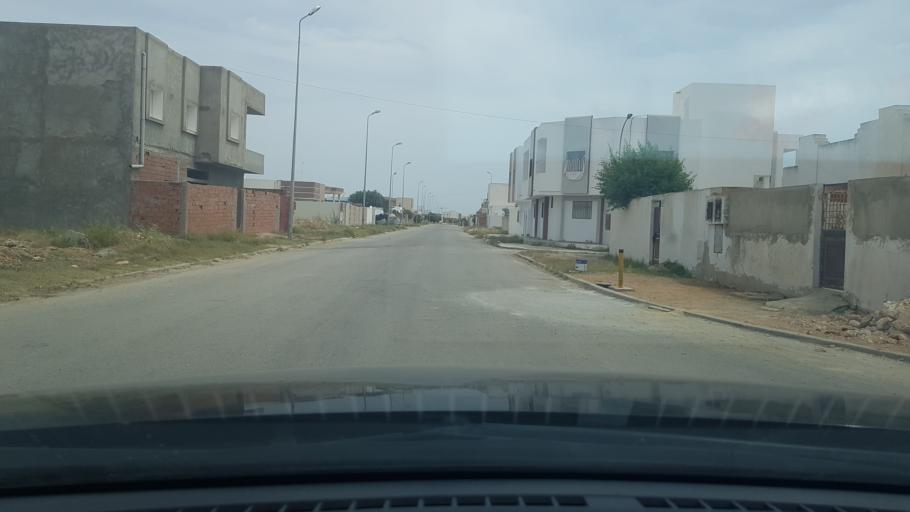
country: TN
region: Safaqis
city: Al Qarmadah
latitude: 34.8255
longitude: 10.7455
